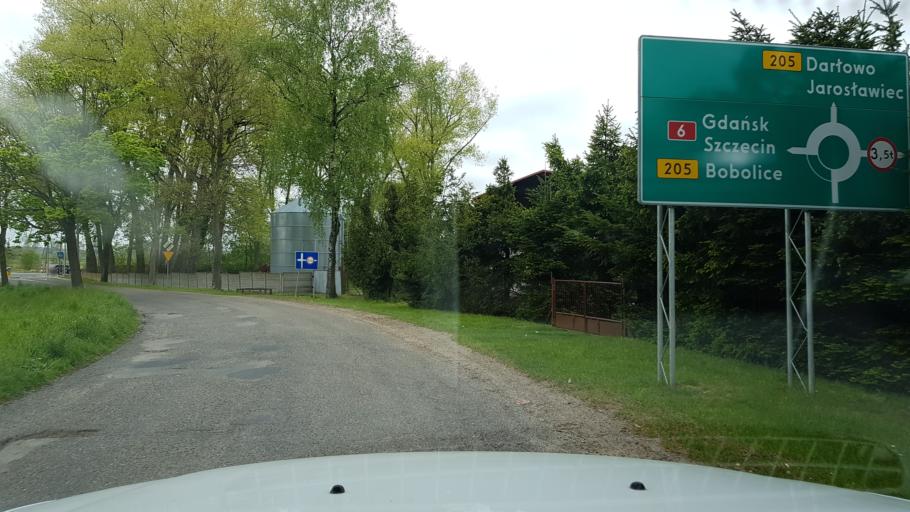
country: PL
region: West Pomeranian Voivodeship
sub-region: Powiat slawienski
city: Slawno
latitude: 54.3697
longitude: 16.6761
